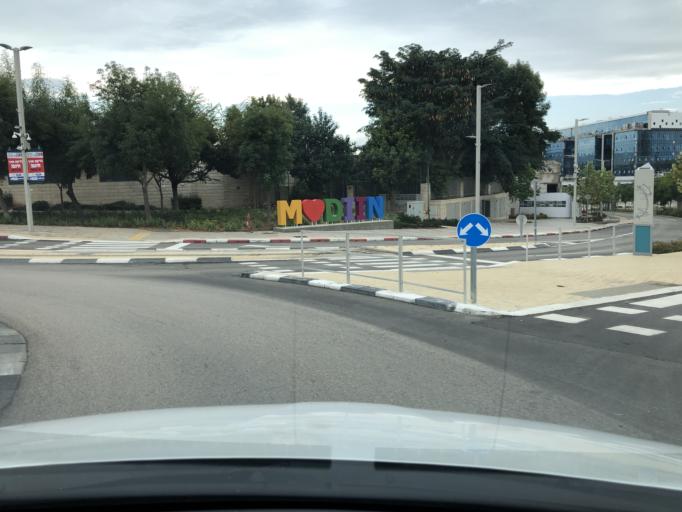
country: IL
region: Central District
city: Modiin
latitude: 31.9077
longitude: 35.0069
